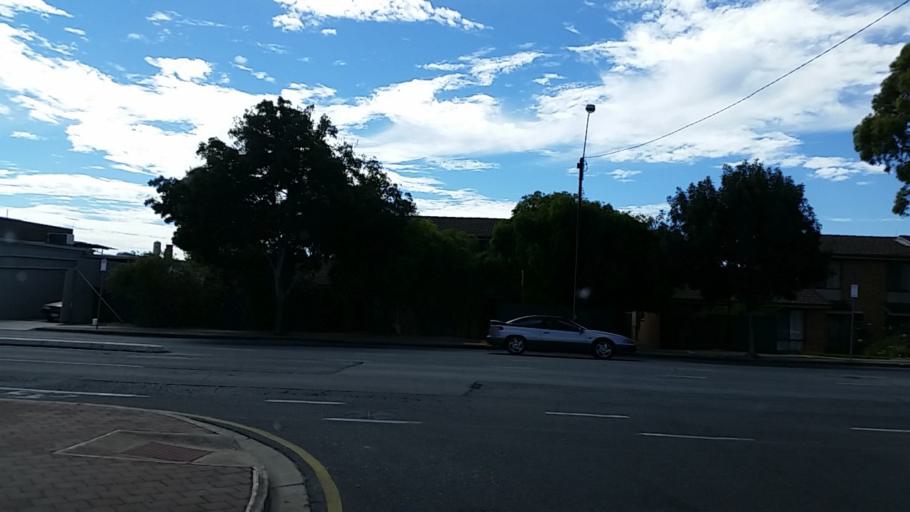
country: AU
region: South Australia
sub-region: Campbelltown
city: Paradise
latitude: -34.8750
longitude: 138.6673
